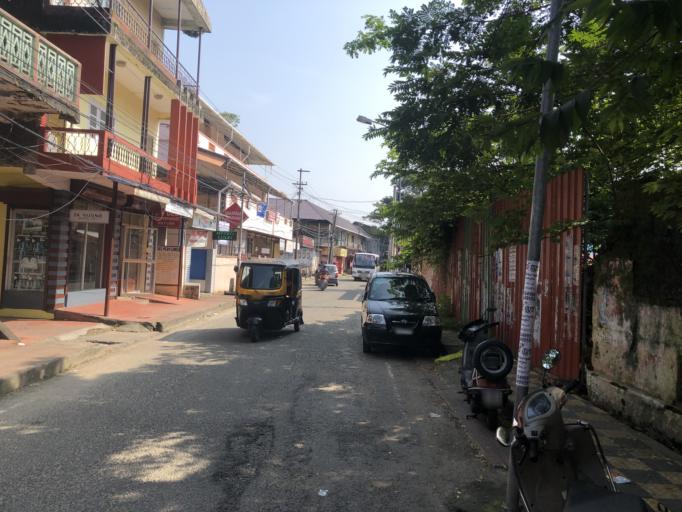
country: IN
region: Kerala
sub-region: Ernakulam
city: Cochin
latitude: 9.9592
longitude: 76.2554
